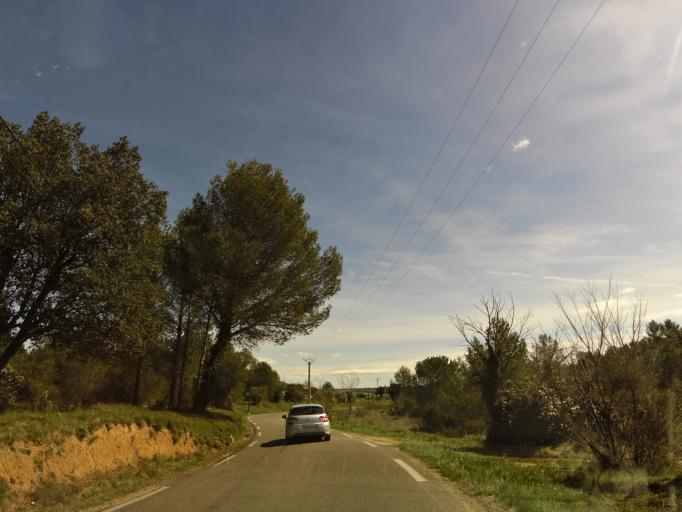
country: FR
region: Languedoc-Roussillon
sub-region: Departement du Gard
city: Bernis
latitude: 43.7782
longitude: 4.2793
